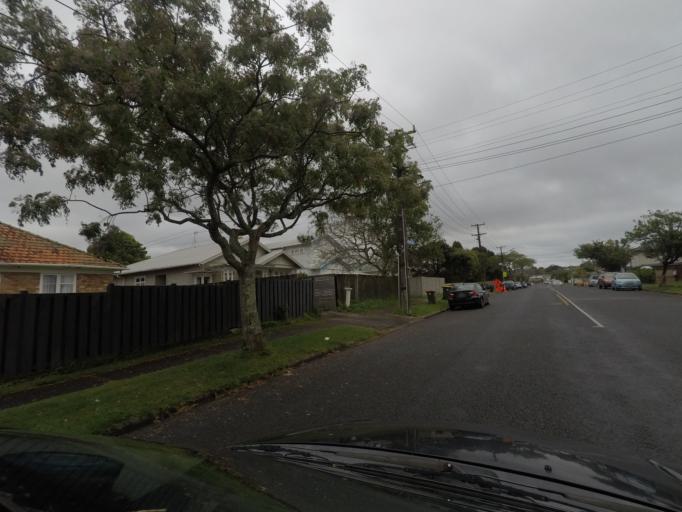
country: NZ
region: Auckland
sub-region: Auckland
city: Auckland
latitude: -36.8878
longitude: 174.7327
